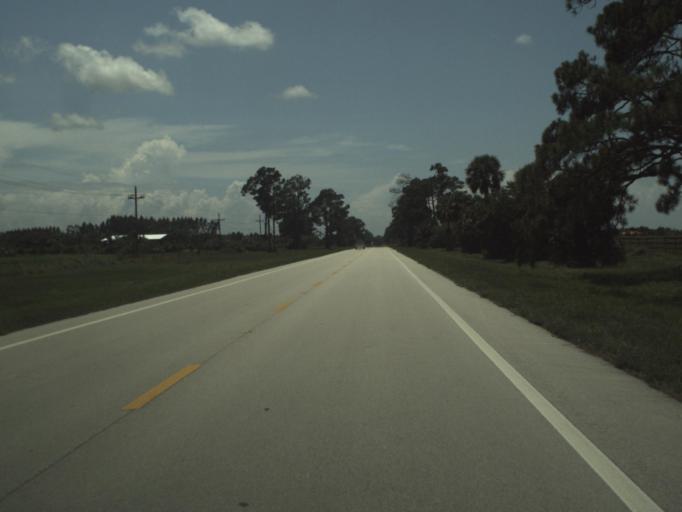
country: US
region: Florida
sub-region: Martin County
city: Indiantown
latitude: 27.0444
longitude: -80.3559
